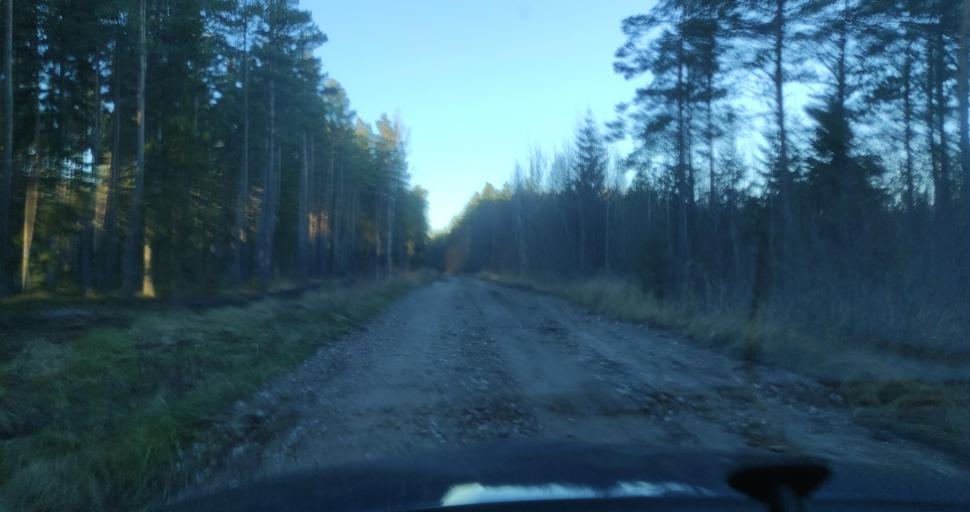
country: LV
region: Dundaga
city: Dundaga
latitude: 57.3809
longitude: 22.0815
